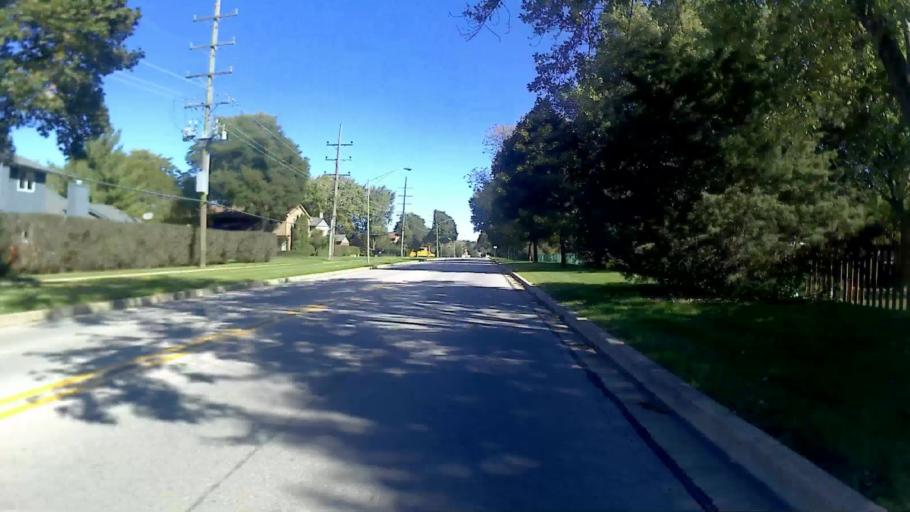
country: US
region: Illinois
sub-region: DuPage County
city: Wheaton
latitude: 41.8484
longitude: -88.0897
